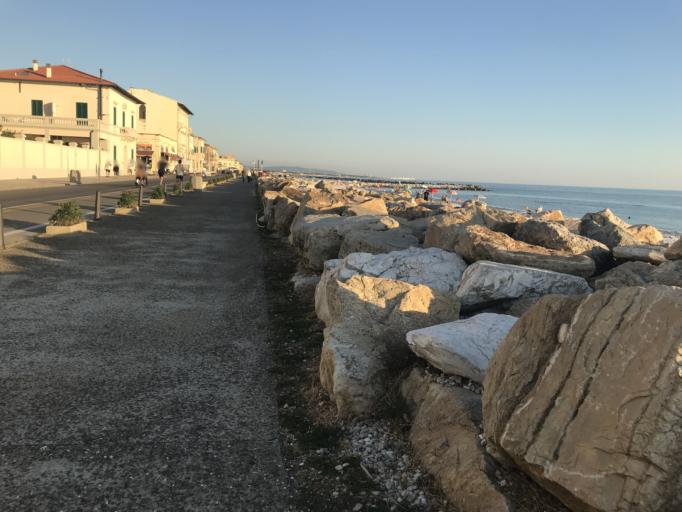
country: IT
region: Tuscany
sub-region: Province of Pisa
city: Marina di Pisa
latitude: 43.6662
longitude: 10.2758
